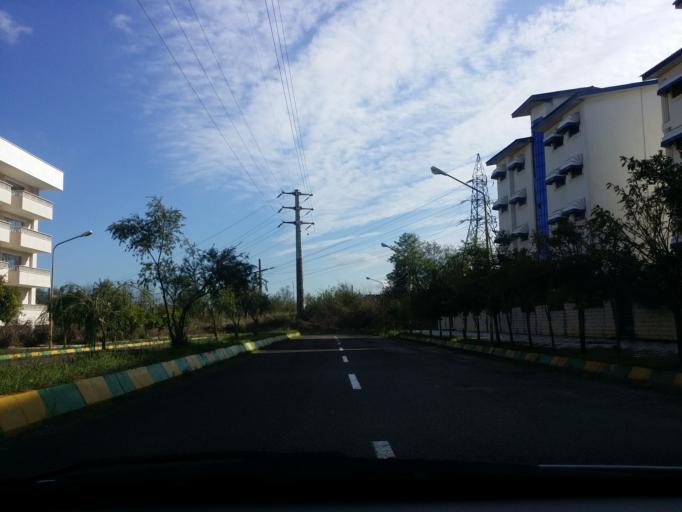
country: IR
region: Mazandaran
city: Chalus
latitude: 36.6741
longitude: 51.3130
